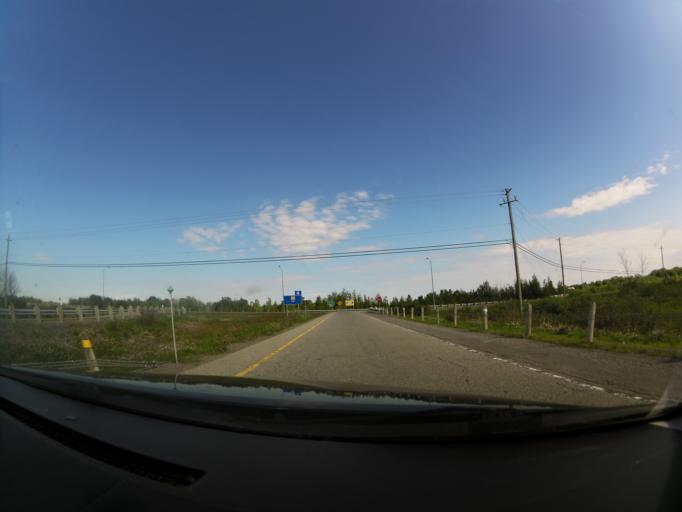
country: CA
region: Ontario
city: Carleton Place
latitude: 45.3139
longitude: -76.0538
